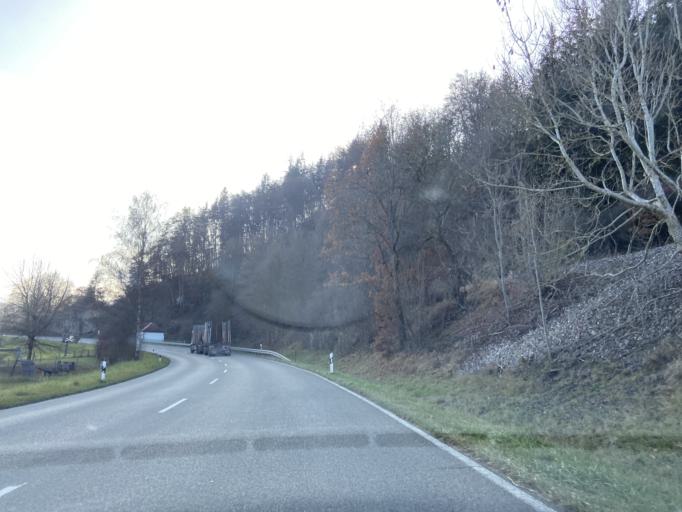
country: DE
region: Baden-Wuerttemberg
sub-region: Tuebingen Region
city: Veringenstadt
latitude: 48.1574
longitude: 9.1999
